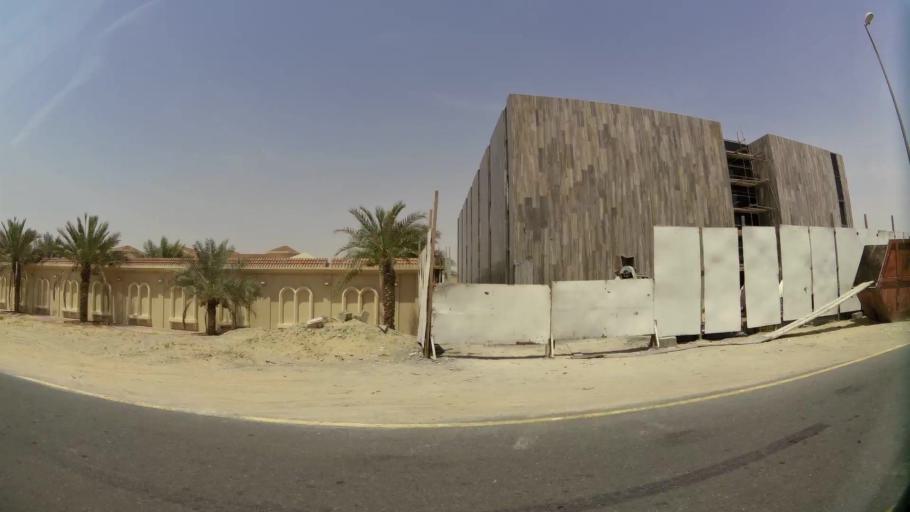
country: AE
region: Ash Shariqah
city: Sharjah
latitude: 25.2458
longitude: 55.5012
